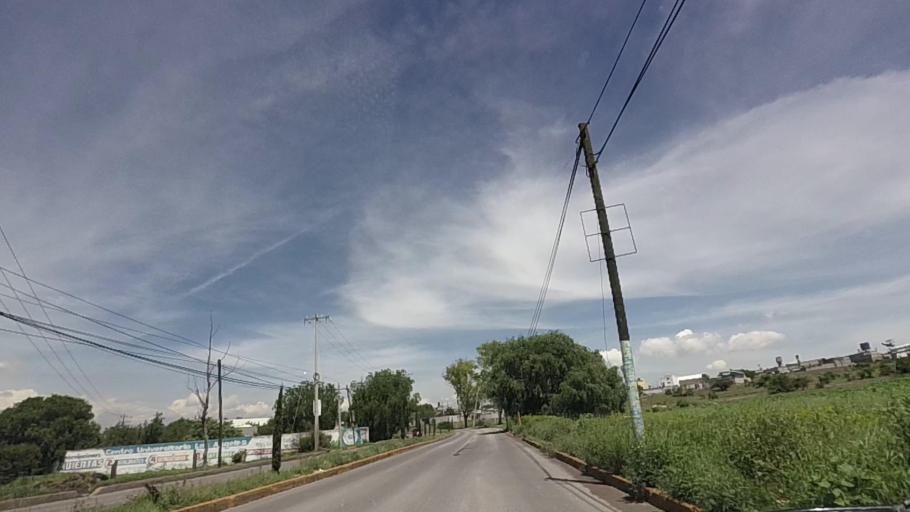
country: MX
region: Mexico
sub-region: Huehuetoca
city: Jorobas
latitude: 19.8261
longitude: -99.2418
